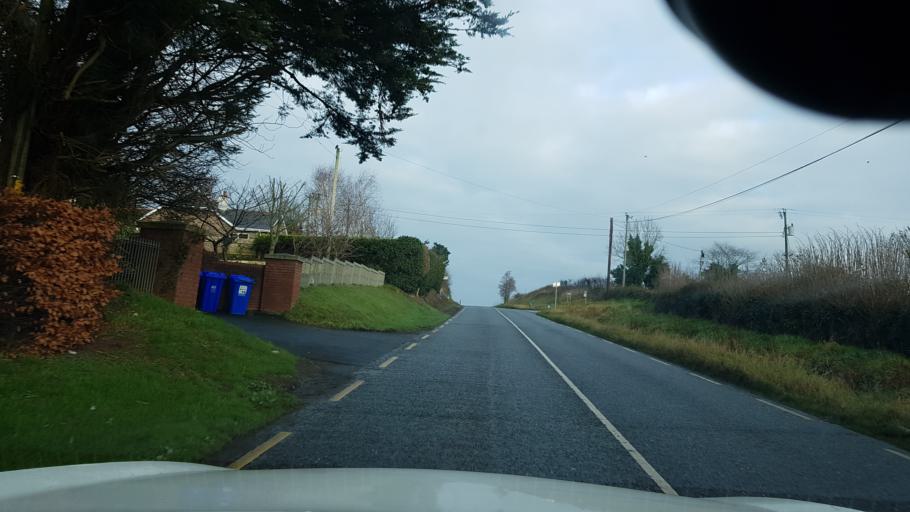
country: IE
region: Leinster
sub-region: An Mhi
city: Navan
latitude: 53.6794
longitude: -6.6749
